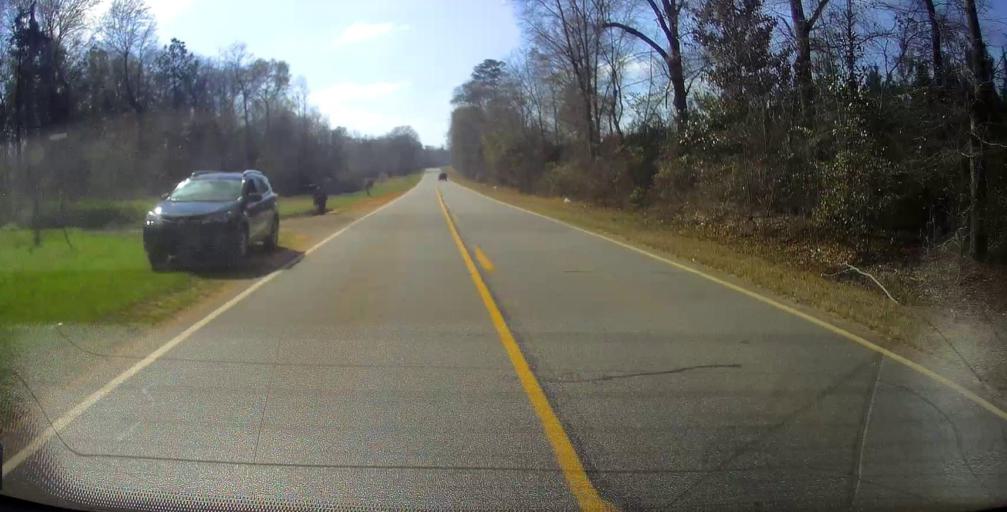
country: US
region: Georgia
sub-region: Twiggs County
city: Jeffersonville
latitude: 32.6816
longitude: -83.2765
